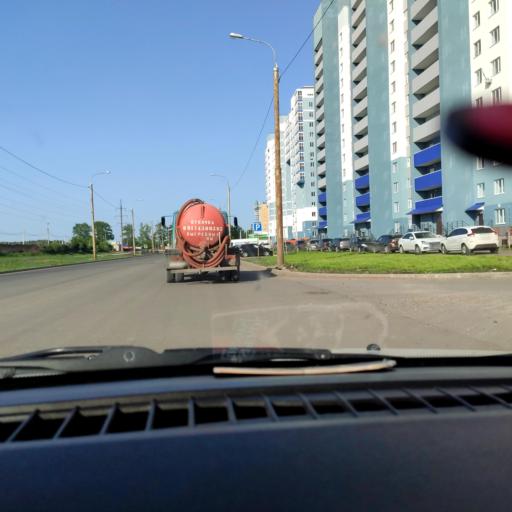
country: RU
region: Bashkortostan
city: Sterlitamak
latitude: 53.6393
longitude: 55.8942
